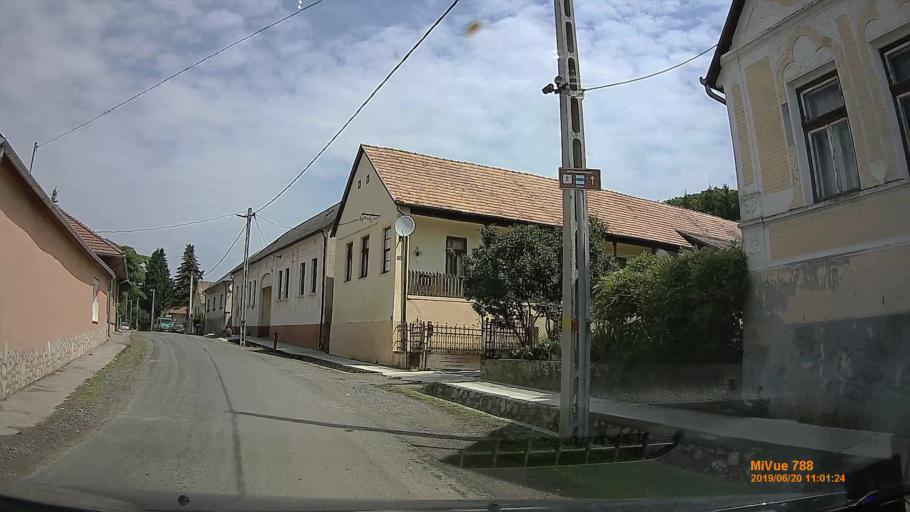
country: HU
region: Baranya
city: Mecseknadasd
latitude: 46.1755
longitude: 18.5121
